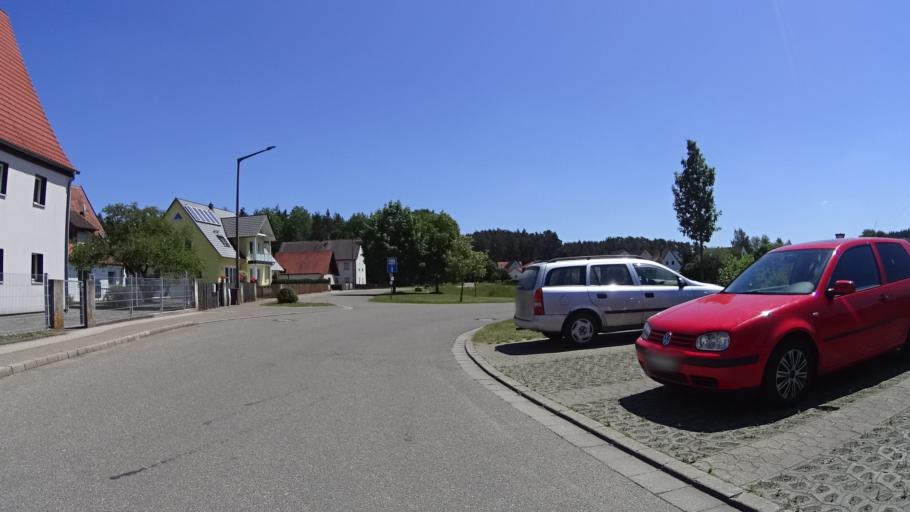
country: DE
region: Bavaria
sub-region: Regierungsbezirk Mittelfranken
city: Pleinfeld
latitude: 49.1029
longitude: 10.9568
